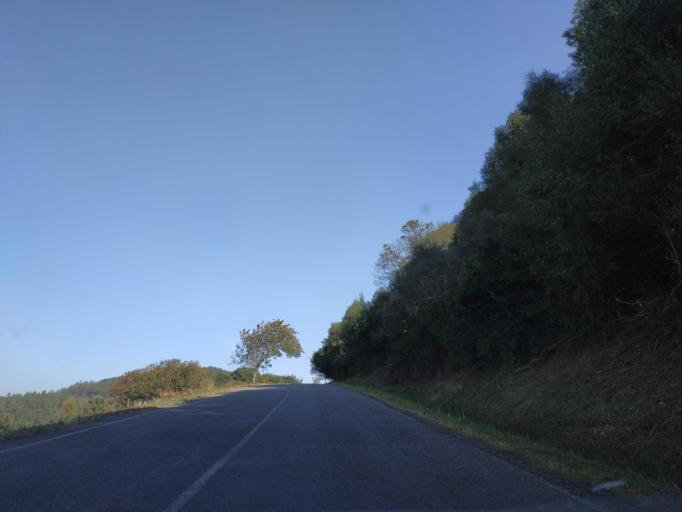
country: ES
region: Galicia
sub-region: Provincia da Coruna
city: Laracha
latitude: 43.2281
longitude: -8.5535
